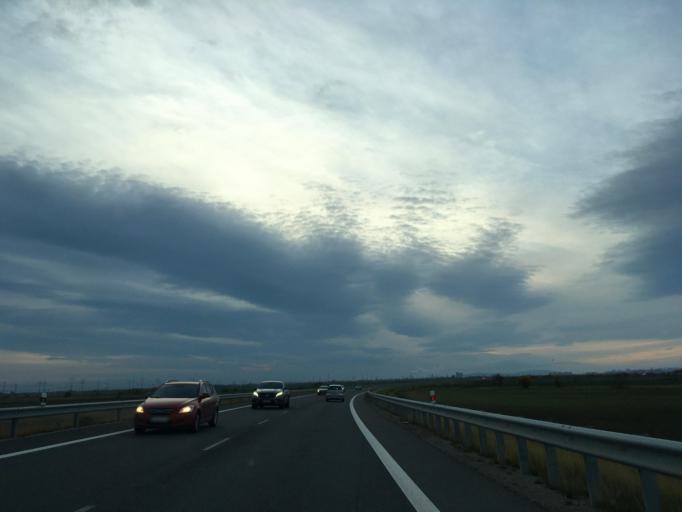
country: SK
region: Bratislavsky
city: Dunajska Luzna
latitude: 48.1285
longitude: 17.2802
